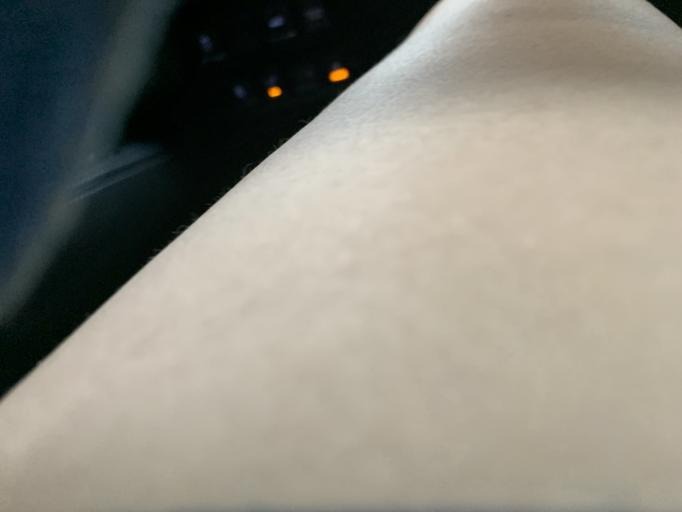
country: US
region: Louisiana
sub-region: Orleans Parish
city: New Orleans
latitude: 29.9812
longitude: -90.1047
